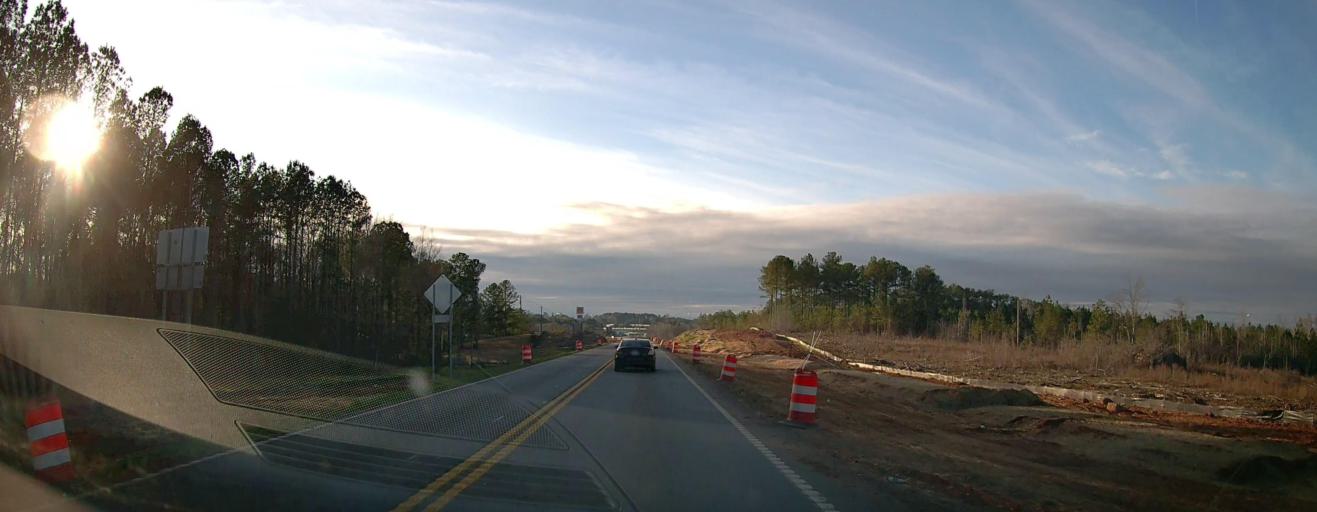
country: US
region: Georgia
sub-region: Troup County
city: West Point
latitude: 32.8754
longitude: -85.1451
